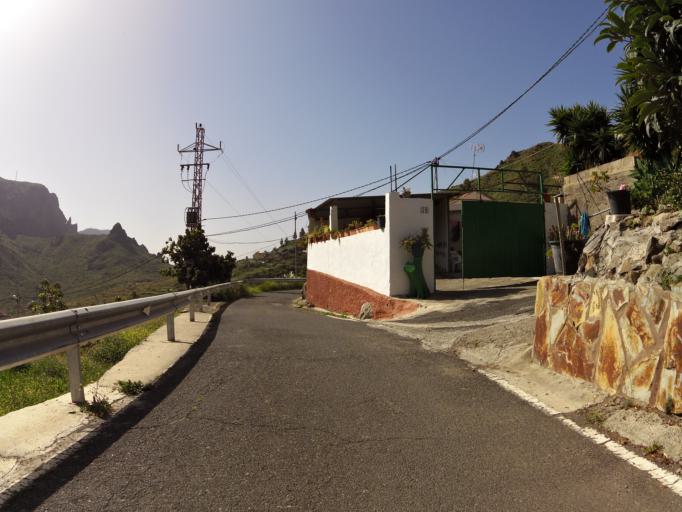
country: ES
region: Canary Islands
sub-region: Provincia de Las Palmas
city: Mogan
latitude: 27.9120
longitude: -15.6677
